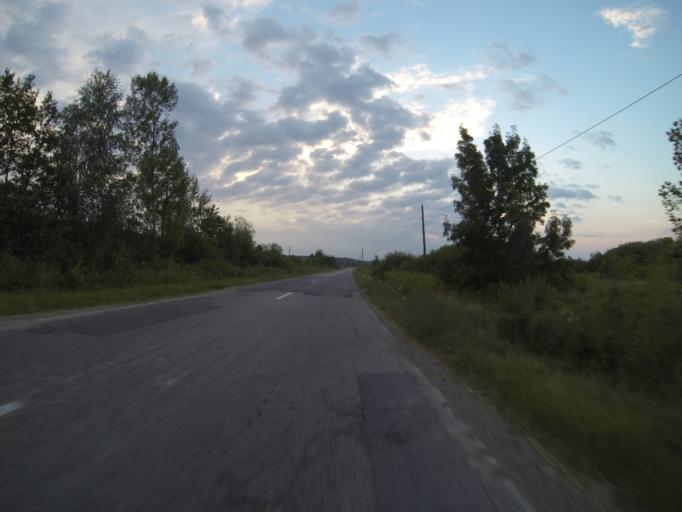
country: RO
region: Brasov
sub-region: Comuna Sinca Veche
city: Persani
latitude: 45.7442
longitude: 25.2004
